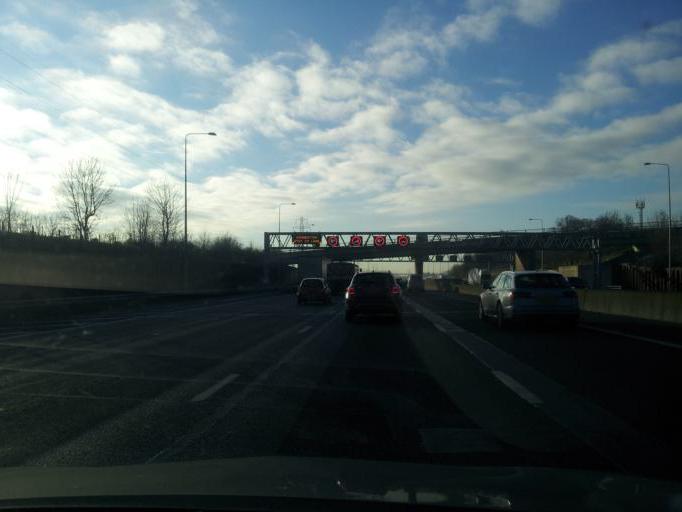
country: GB
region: England
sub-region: Buckinghamshire
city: Chalfont Saint Peter
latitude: 51.6149
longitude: -0.5263
